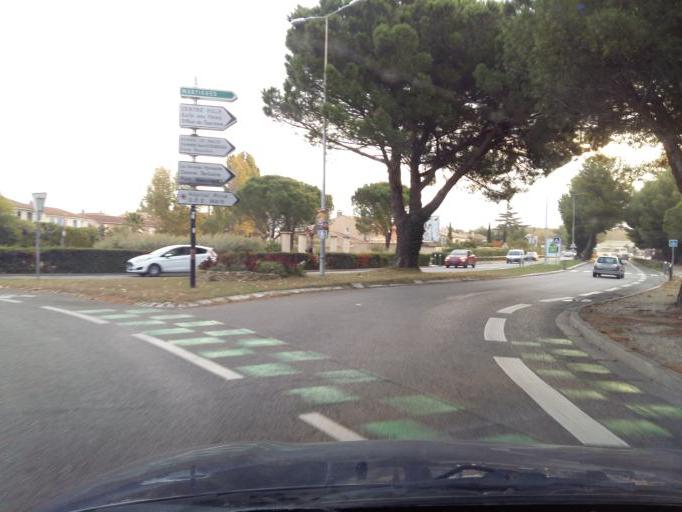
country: FR
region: Provence-Alpes-Cote d'Azur
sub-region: Departement des Bouches-du-Rhone
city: Istres
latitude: 43.4982
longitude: 4.9808
